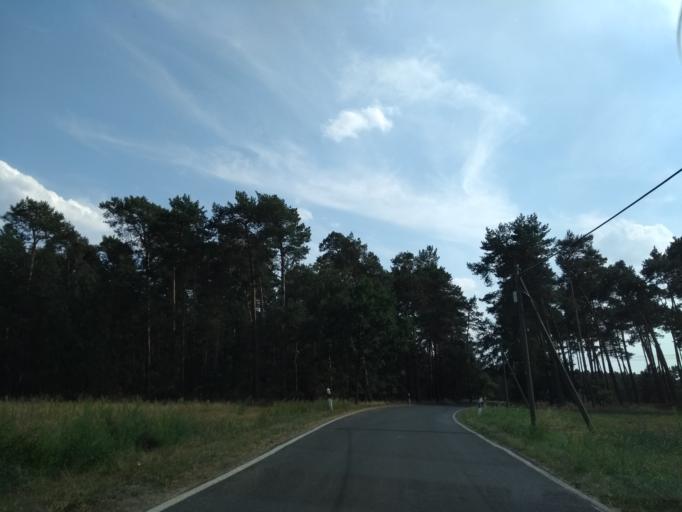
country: DE
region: Brandenburg
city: Luebben
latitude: 51.8642
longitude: 13.8525
